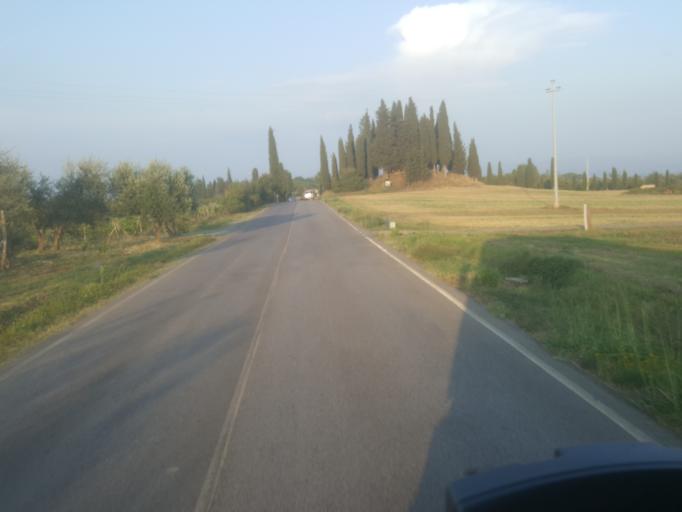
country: IT
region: Tuscany
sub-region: Province of Florence
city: Gambassi Terme
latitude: 43.5307
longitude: 10.9327
